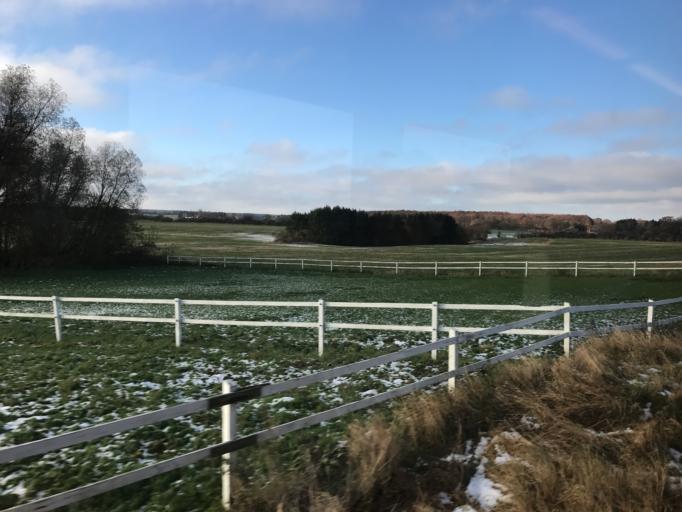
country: DK
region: Zealand
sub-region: Stevns Kommune
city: Harlev
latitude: 55.3764
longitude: 12.2081
